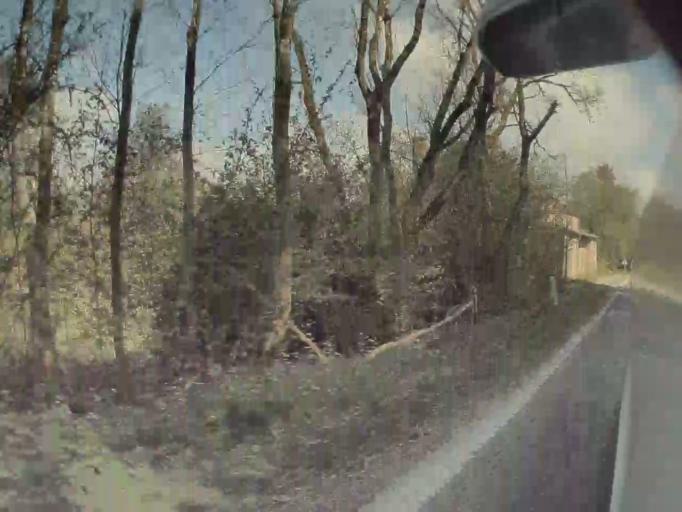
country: BE
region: Wallonia
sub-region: Province du Luxembourg
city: Tellin
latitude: 50.0301
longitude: 5.2067
